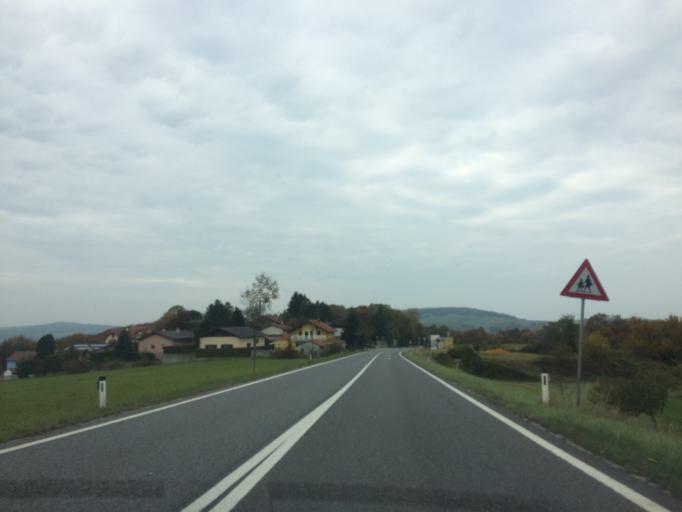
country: AT
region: Lower Austria
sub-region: Politischer Bezirk Tulln
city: Tulbing
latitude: 48.2554
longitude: 16.0871
